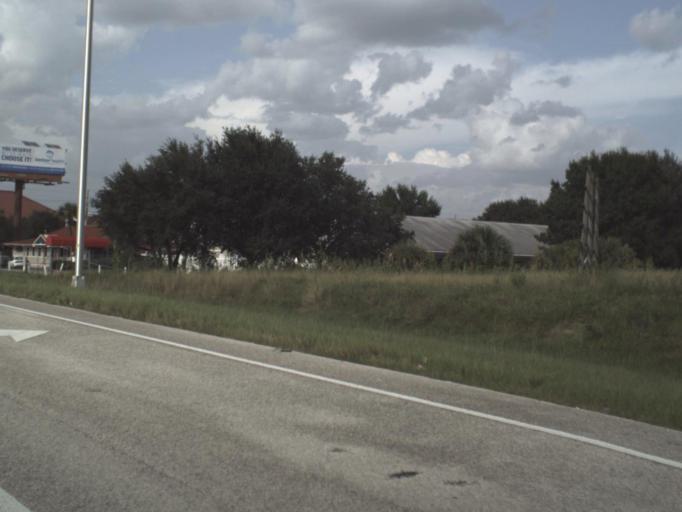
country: US
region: Florida
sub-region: Polk County
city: Davenport
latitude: 28.2127
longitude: -81.6397
